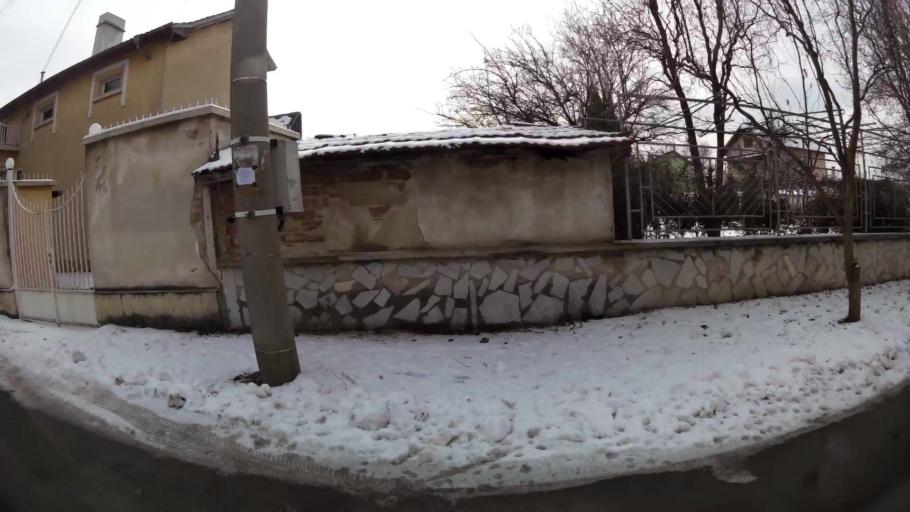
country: BG
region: Sofia-Capital
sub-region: Stolichna Obshtina
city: Sofia
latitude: 42.7118
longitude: 23.4175
